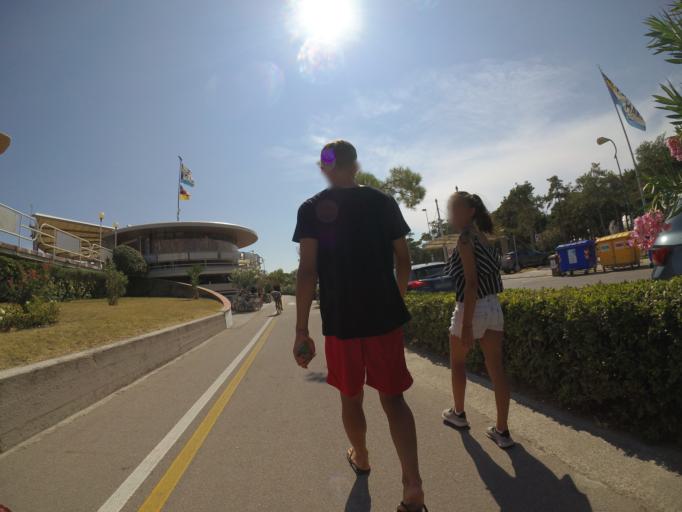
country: IT
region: Friuli Venezia Giulia
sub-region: Provincia di Udine
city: Lignano Sabbiadoro
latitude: 45.6646
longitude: 13.1097
